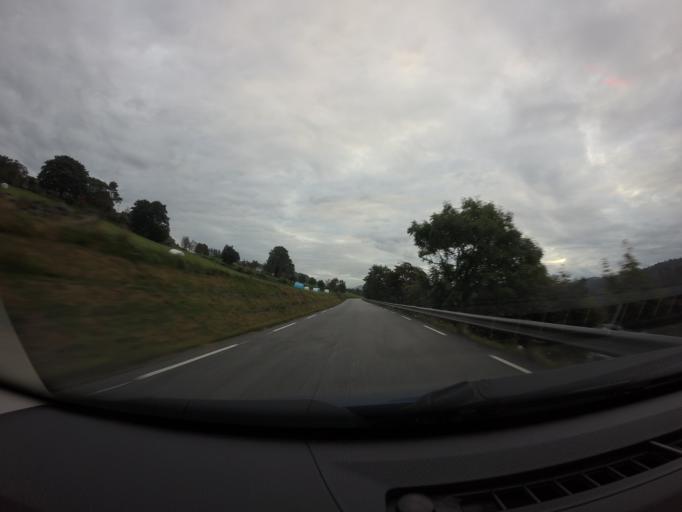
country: NO
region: Rogaland
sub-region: Gjesdal
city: Algard
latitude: 58.7702
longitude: 5.8926
